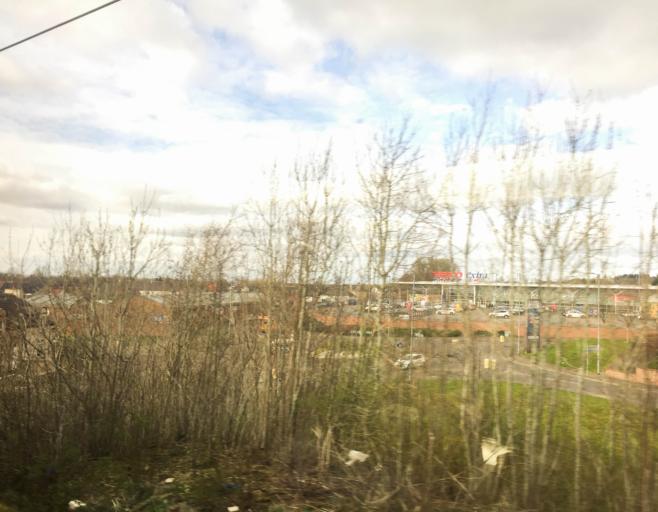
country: GB
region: Scotland
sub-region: North Lanarkshire
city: Wishaw
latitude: 55.7730
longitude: -3.9284
